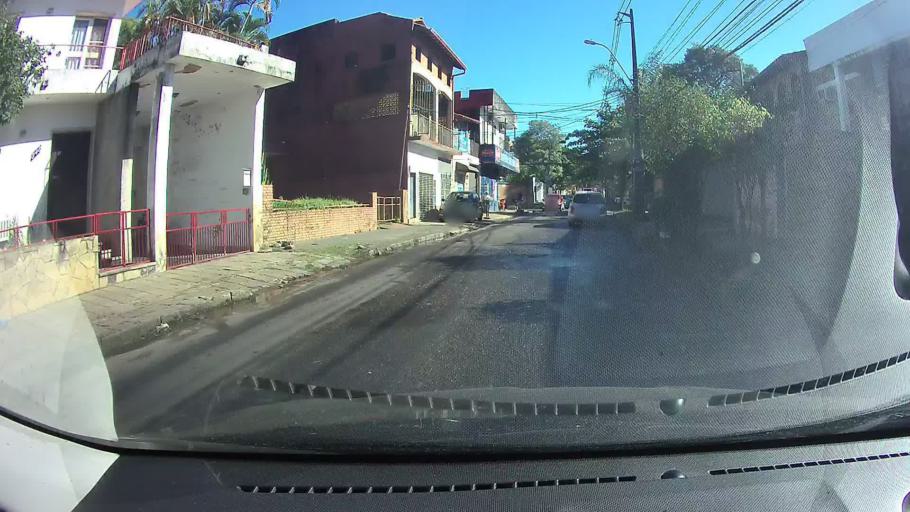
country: PY
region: Asuncion
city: Asuncion
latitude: -25.2930
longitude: -57.5952
